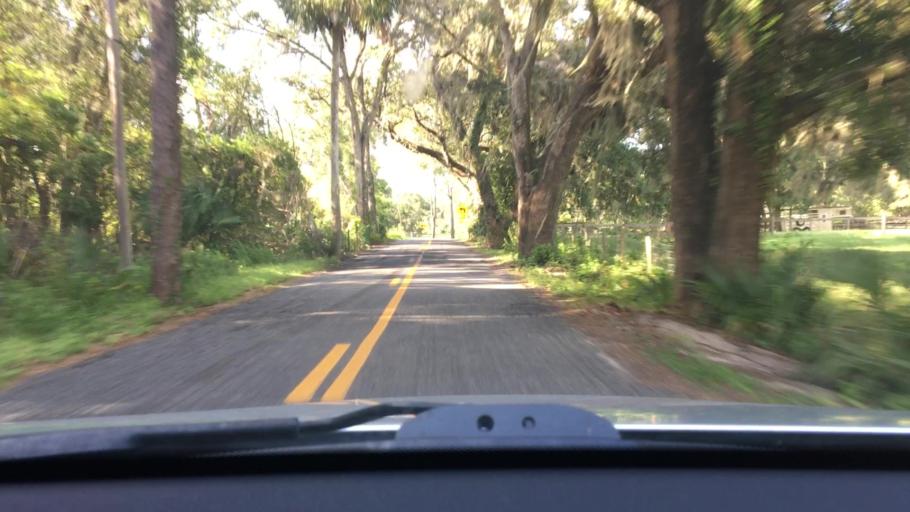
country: US
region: Florida
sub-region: Volusia County
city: Lake Helen
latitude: 28.9692
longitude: -81.2151
